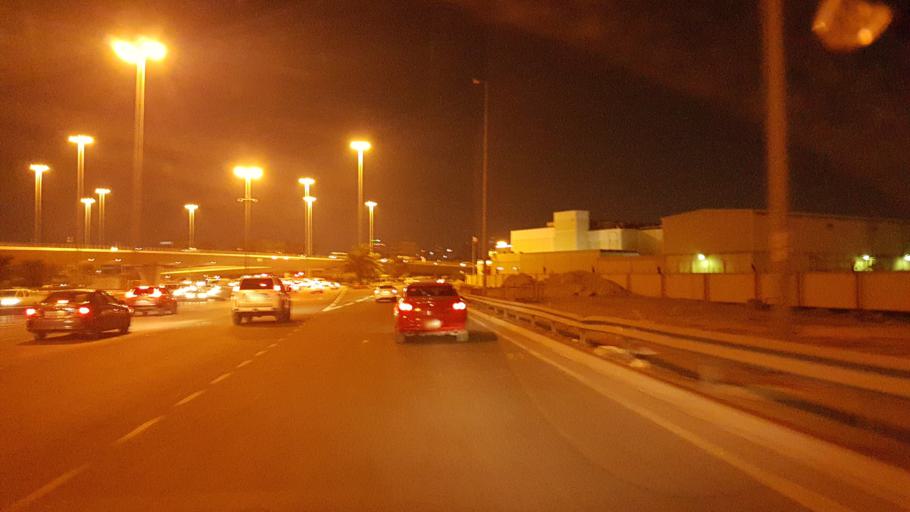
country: BH
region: Manama
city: Manama
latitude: 26.1963
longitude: 50.5902
